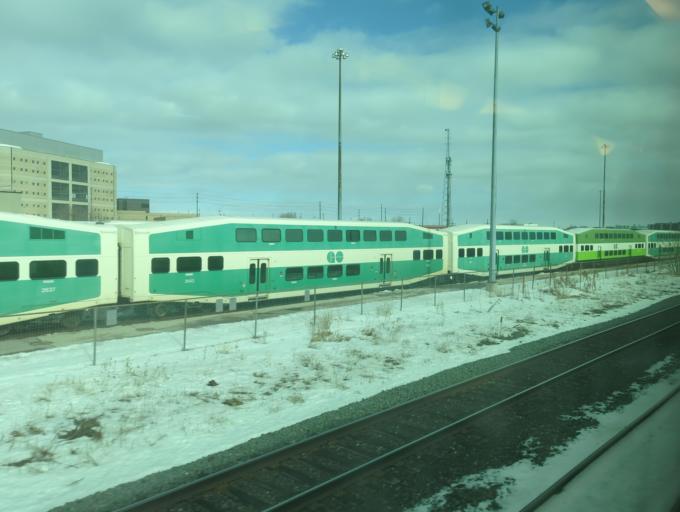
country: CA
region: Ontario
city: Etobicoke
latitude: 43.6068
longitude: -79.5156
